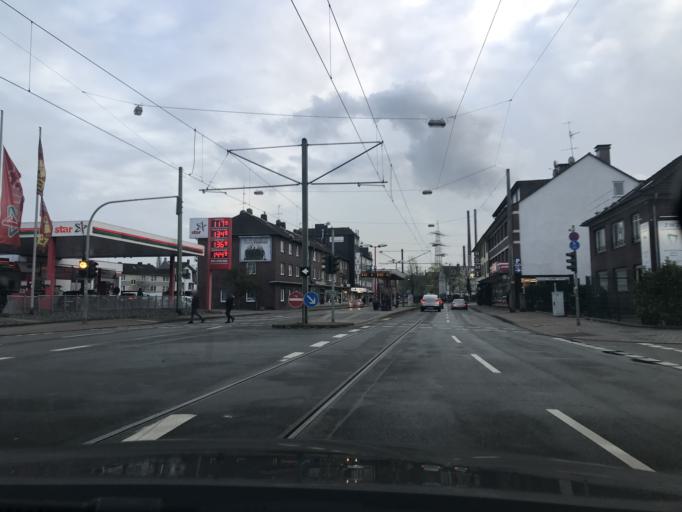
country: DE
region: North Rhine-Westphalia
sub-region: Regierungsbezirk Dusseldorf
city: Dinslaken
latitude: 51.5180
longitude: 6.7413
